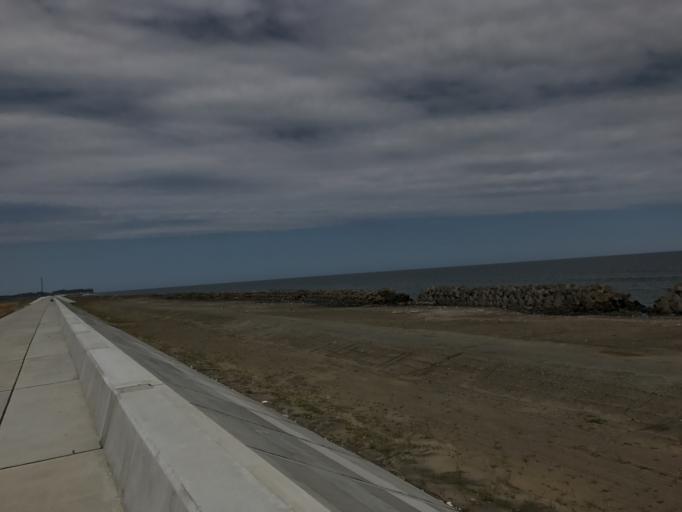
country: JP
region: Miyagi
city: Marumori
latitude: 37.7849
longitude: 140.9868
